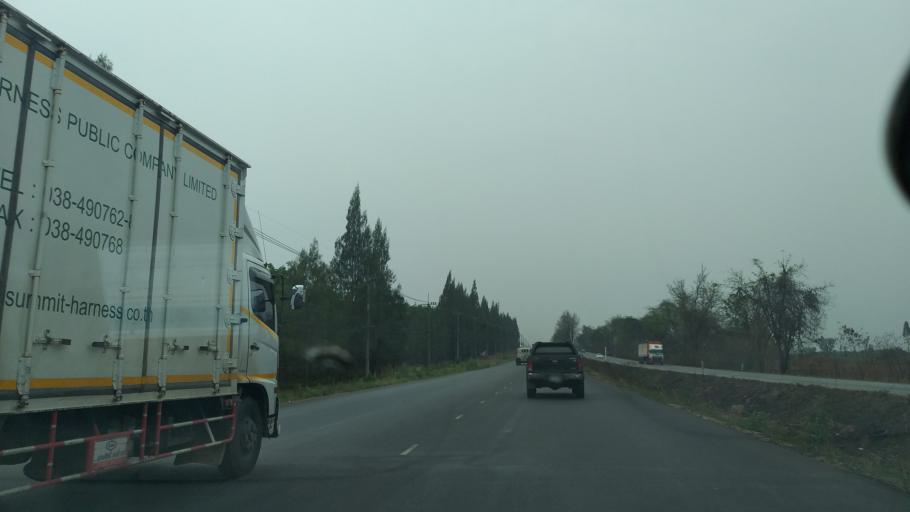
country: TH
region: Chachoengsao
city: Plaeng Yao
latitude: 13.5158
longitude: 101.2671
